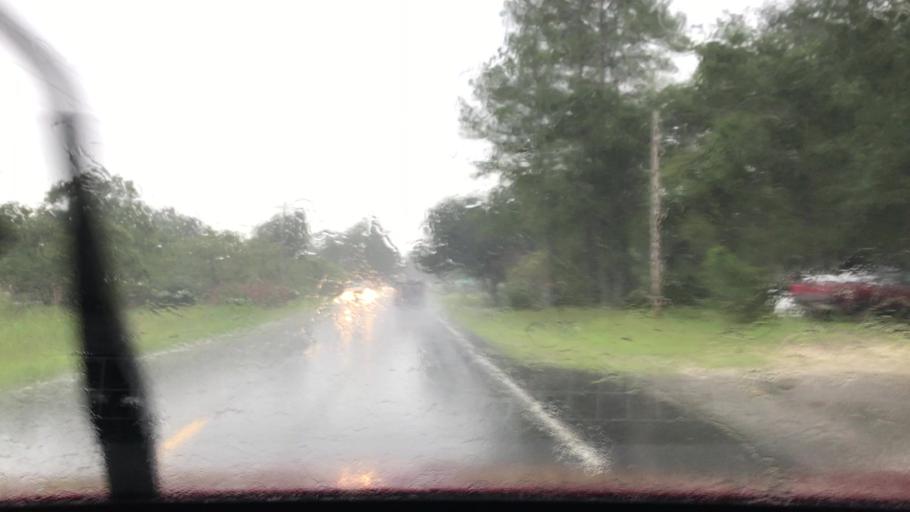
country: US
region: South Carolina
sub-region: Horry County
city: Red Hill
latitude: 33.9021
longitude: -78.8896
